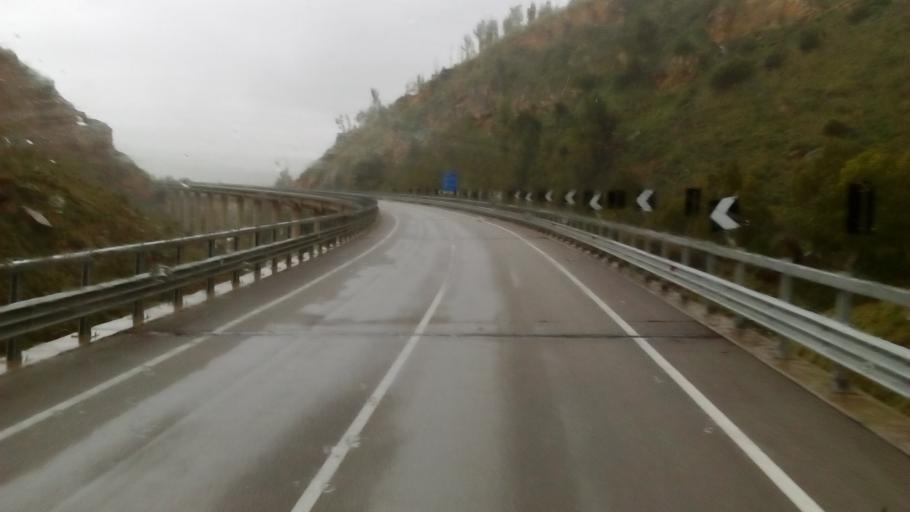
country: IT
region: Sicily
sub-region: Enna
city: Pietraperzia
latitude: 37.5002
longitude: 14.1411
